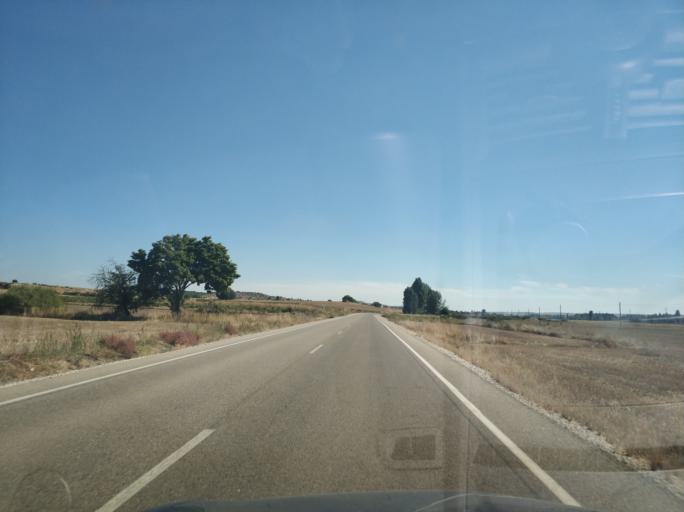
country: ES
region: Castille and Leon
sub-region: Provincia de Burgos
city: Zazuar
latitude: 41.6939
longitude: -3.5414
